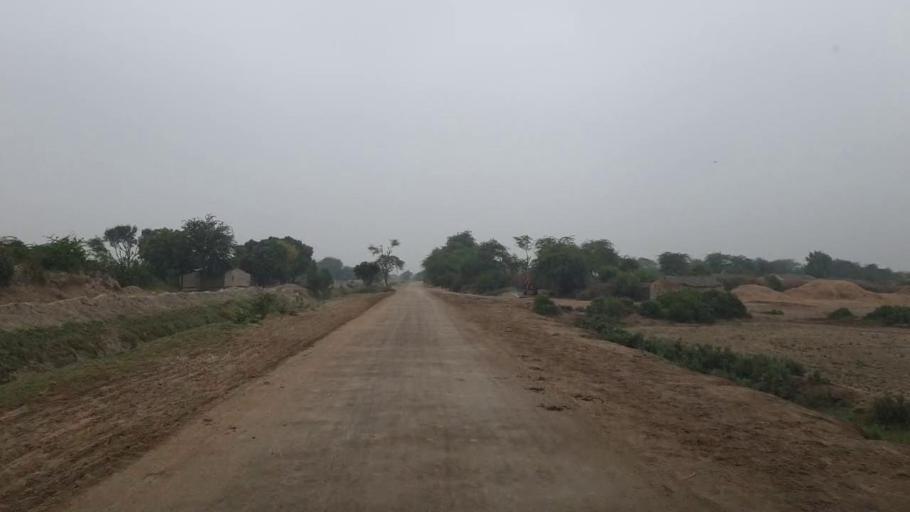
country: PK
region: Sindh
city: Badin
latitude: 24.6024
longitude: 68.6754
